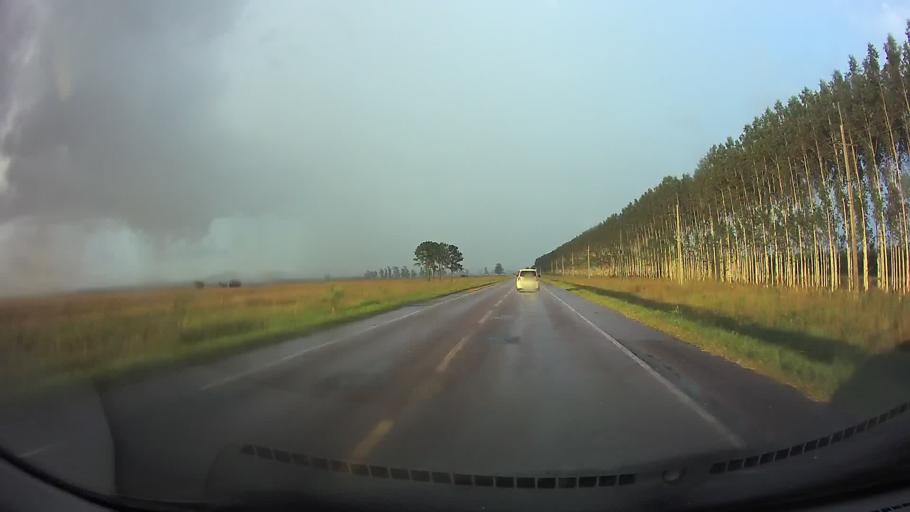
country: PY
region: Paraguari
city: Paraguari
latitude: -25.6689
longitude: -57.1647
